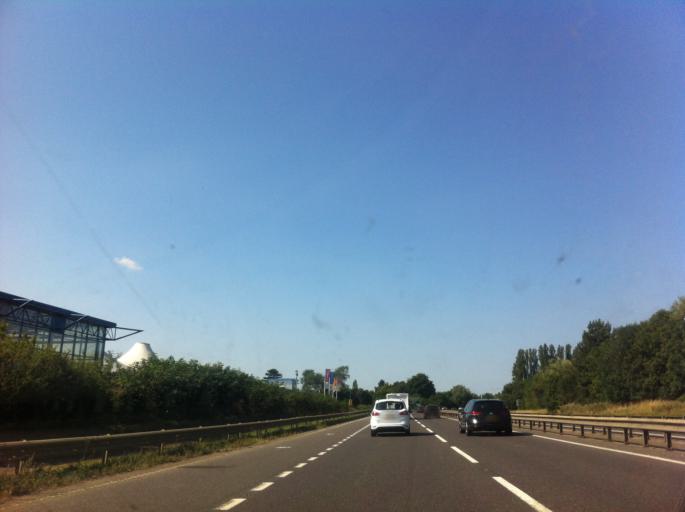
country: GB
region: England
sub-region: Northamptonshire
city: Earls Barton
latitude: 52.2502
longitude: -0.8111
